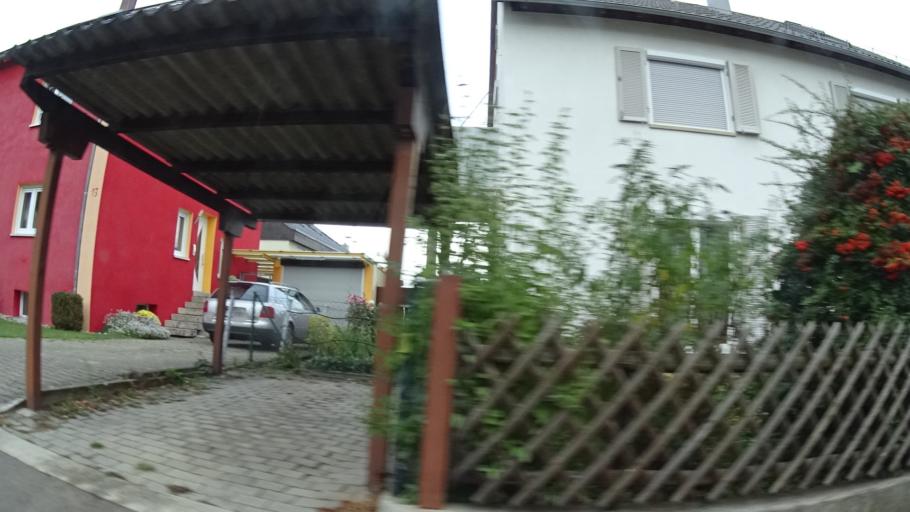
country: DE
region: Baden-Wuerttemberg
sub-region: Regierungsbezirk Stuttgart
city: Gerlingen
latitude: 48.7981
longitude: 9.0682
